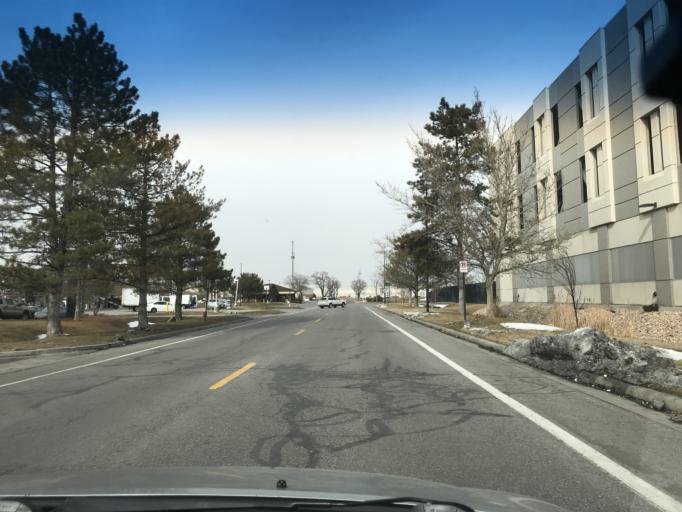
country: US
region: Utah
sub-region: Salt Lake County
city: West Valley City
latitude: 40.7751
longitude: -112.0223
